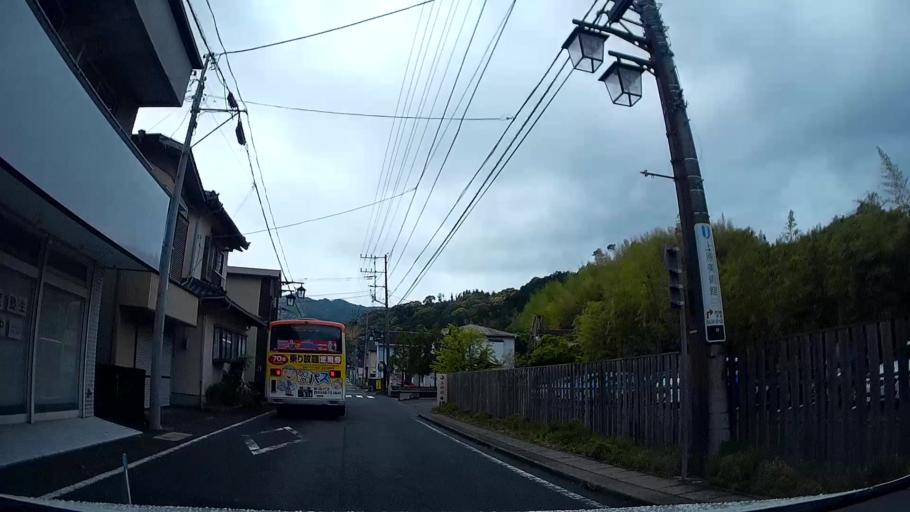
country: JP
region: Shizuoka
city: Shimoda
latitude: 34.7572
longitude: 138.9834
